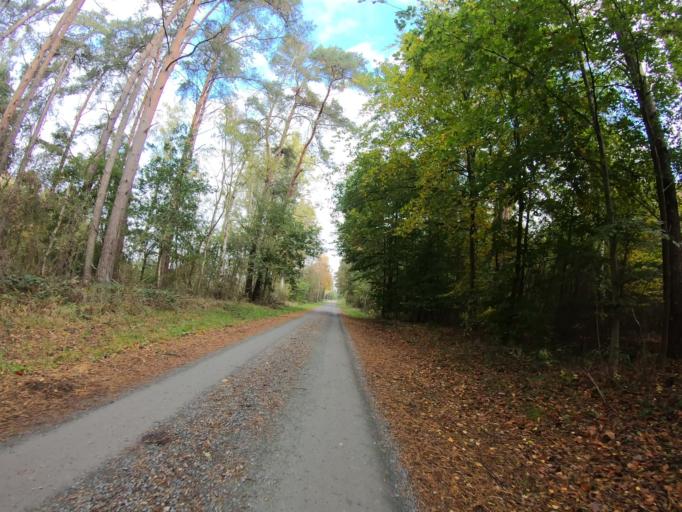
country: DE
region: Lower Saxony
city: Wesendorf
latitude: 52.5686
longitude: 10.5638
